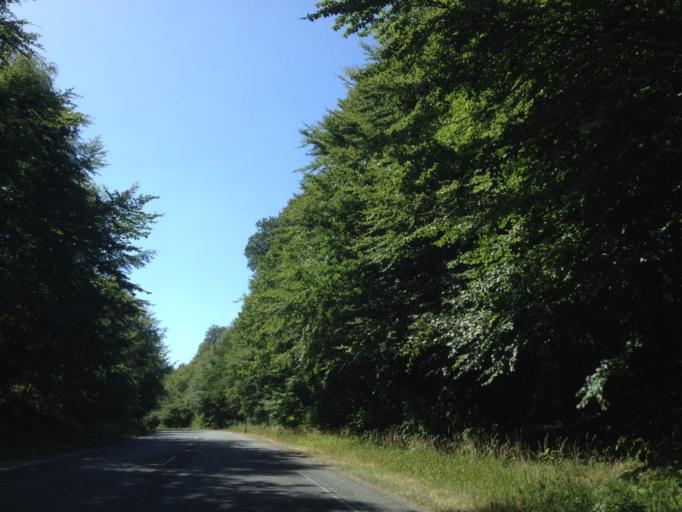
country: DK
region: Capital Region
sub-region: Hillerod Kommune
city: Nodebo
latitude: 56.0435
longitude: 12.3701
